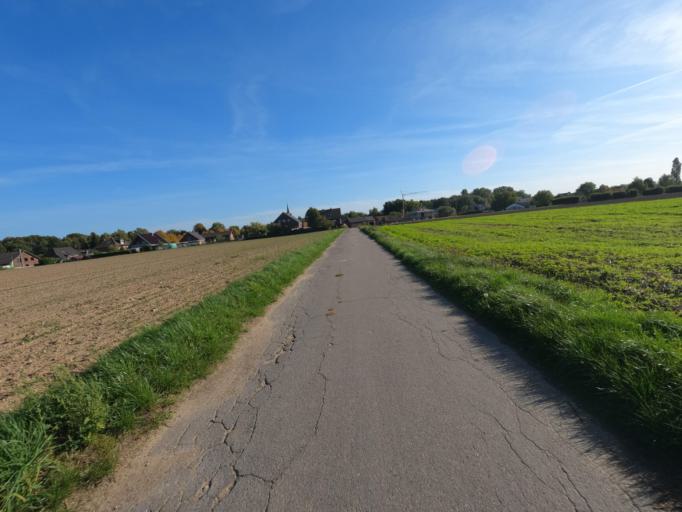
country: DE
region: North Rhine-Westphalia
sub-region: Regierungsbezirk Dusseldorf
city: Niederkruchten
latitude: 51.1767
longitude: 6.2449
